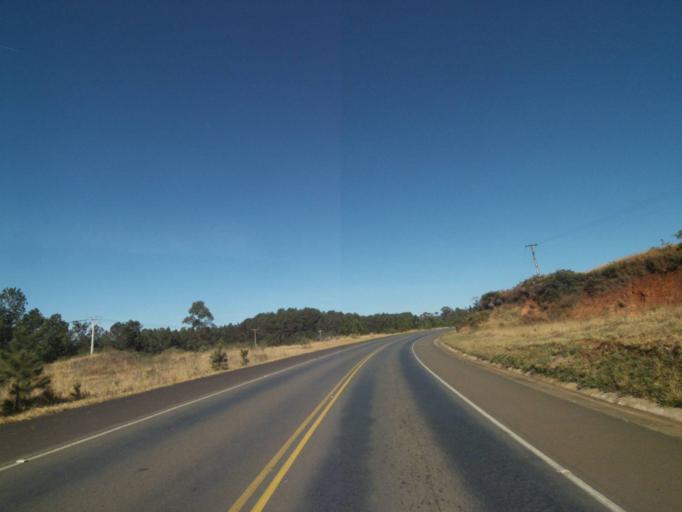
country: BR
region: Parana
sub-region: Tibagi
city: Tibagi
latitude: -24.4892
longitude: -50.4386
